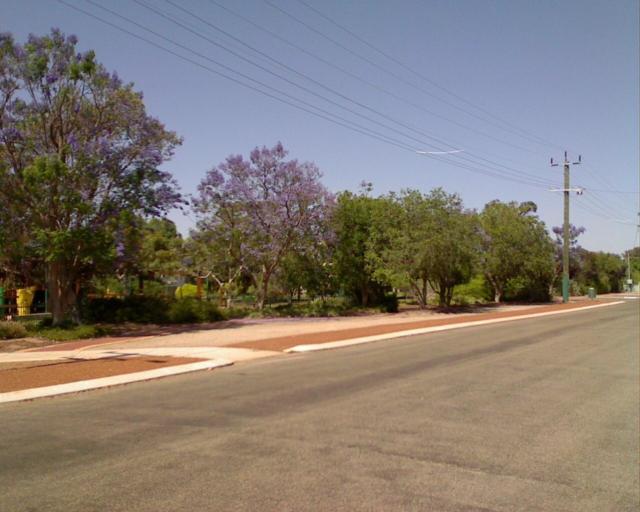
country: AU
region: Western Australia
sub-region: Merredin
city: Merredin
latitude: -30.9156
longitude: 118.2083
